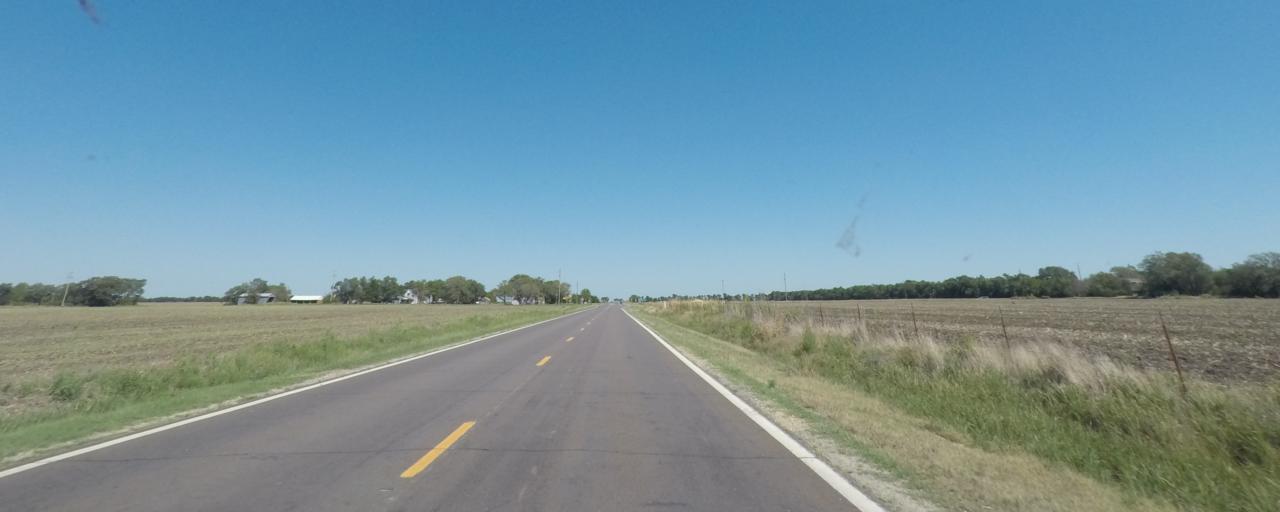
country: US
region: Kansas
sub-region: Sumner County
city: Wellington
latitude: 37.1556
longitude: -97.4023
